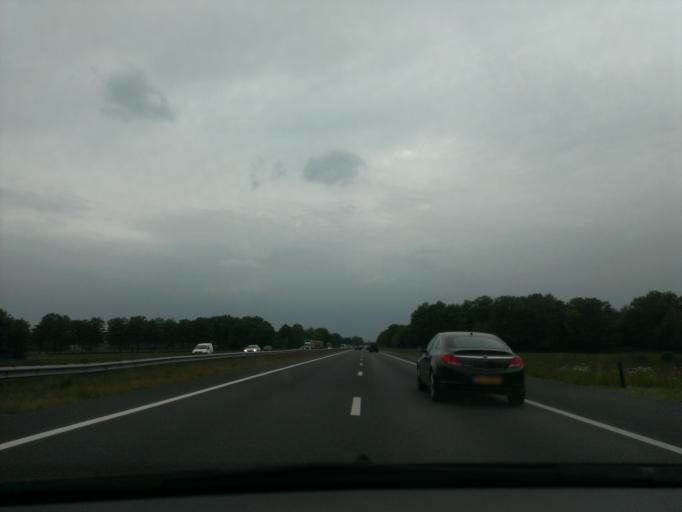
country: NL
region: Overijssel
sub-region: Gemeente Hof van Twente
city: Goor
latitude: 52.2873
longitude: 6.6097
